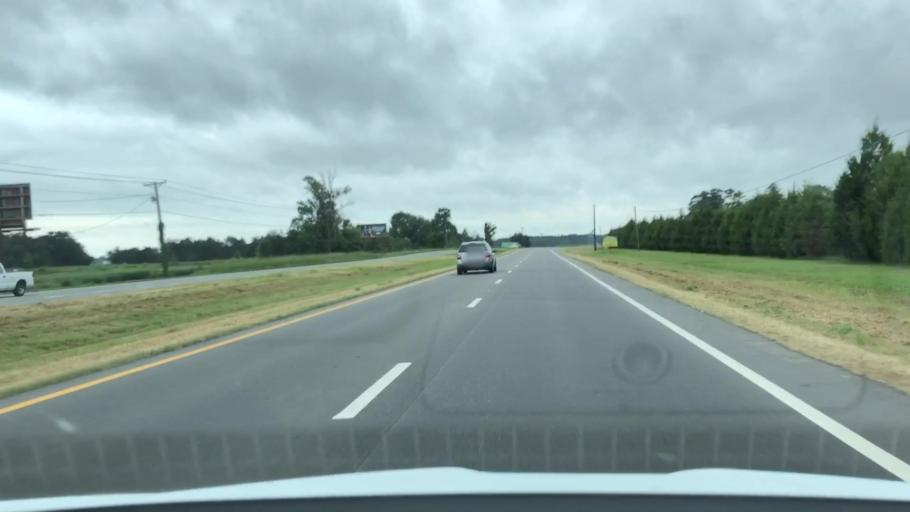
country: US
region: North Carolina
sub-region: Lenoir County
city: La Grange
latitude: 35.2602
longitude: -77.6998
